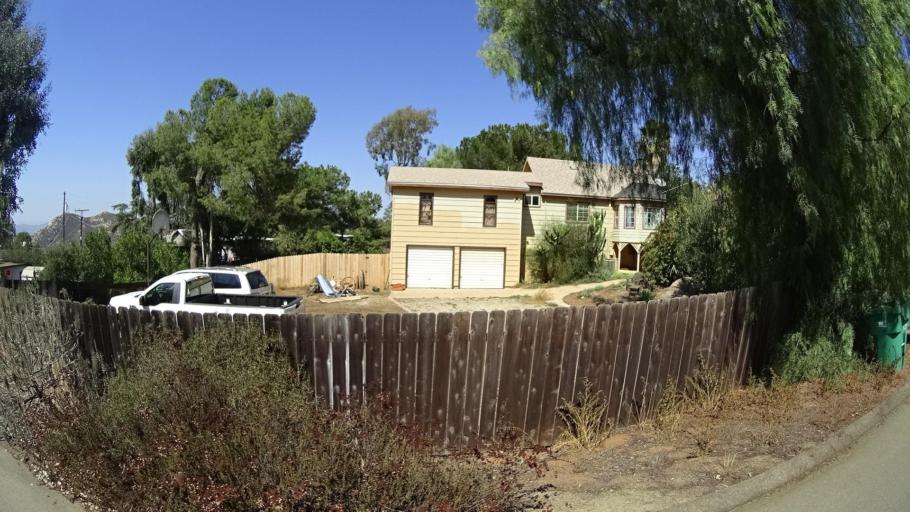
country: US
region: California
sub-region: San Diego County
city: Crest
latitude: 32.8084
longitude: -116.8671
